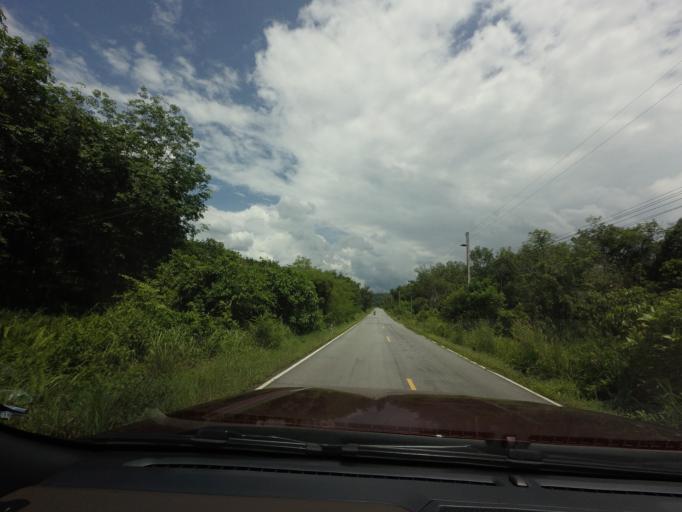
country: TH
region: Narathiwat
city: Chanae
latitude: 6.0648
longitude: 101.6877
